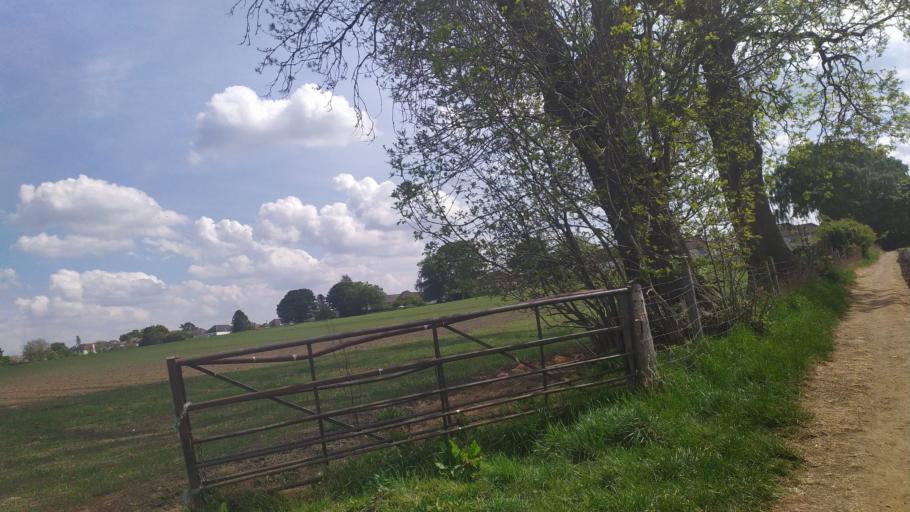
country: GB
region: England
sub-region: City and Borough of Leeds
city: Chapel Allerton
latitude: 53.8650
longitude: -1.5601
